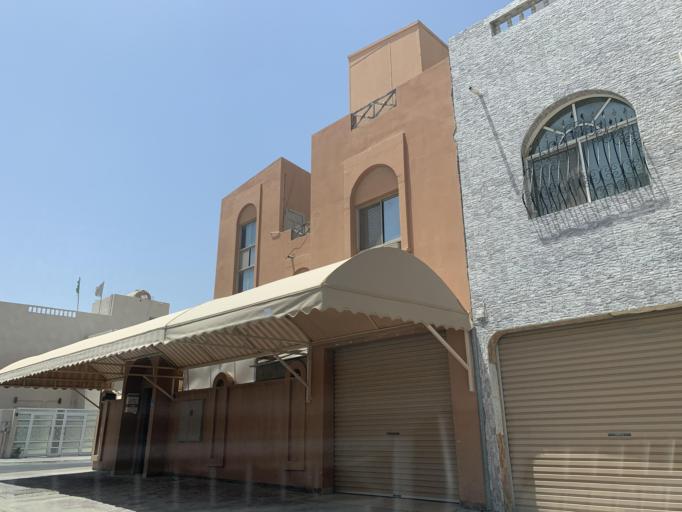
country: BH
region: Northern
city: Ar Rifa'
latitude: 26.1403
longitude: 50.5663
